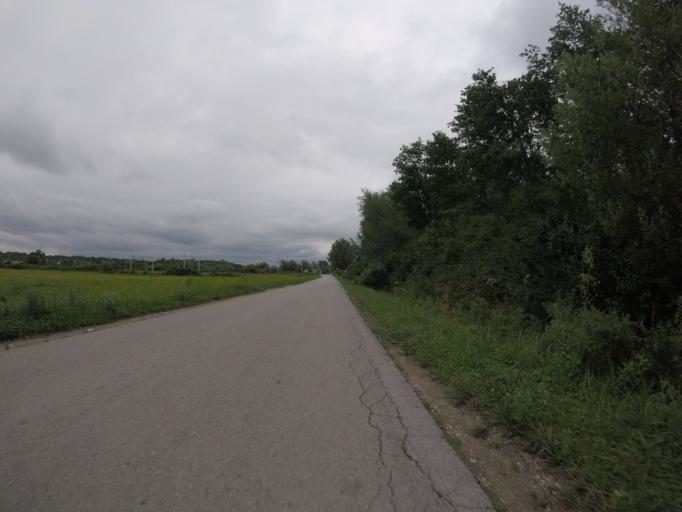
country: HR
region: Zagrebacka
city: Turopolje
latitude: 45.6444
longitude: 16.1337
